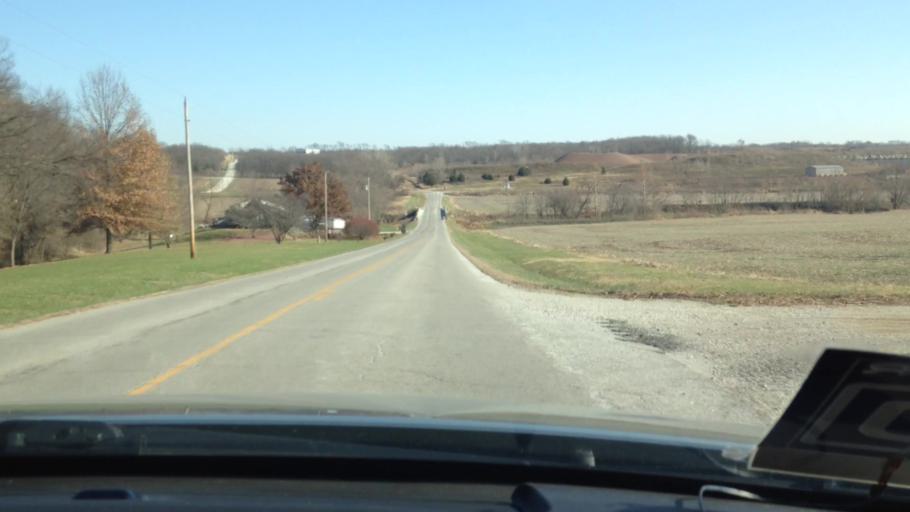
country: US
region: Missouri
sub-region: Platte County
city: Weston
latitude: 39.4982
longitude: -94.8076
